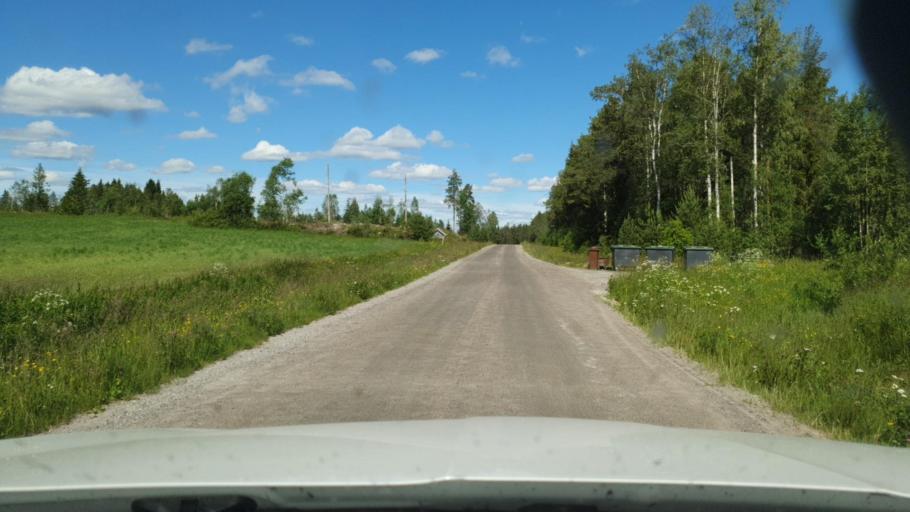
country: SE
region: Vaesterbotten
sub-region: Skelleftea Kommun
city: Byske
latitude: 65.1239
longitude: 21.2045
